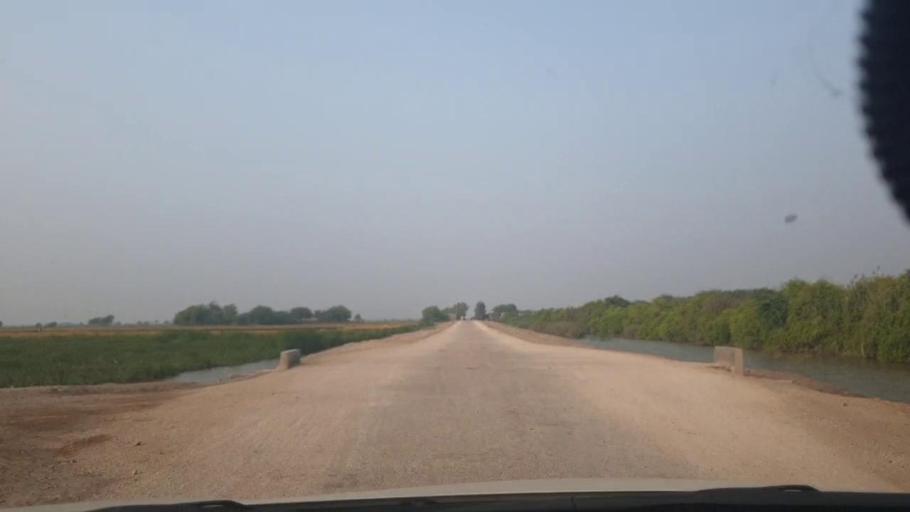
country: PK
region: Sindh
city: Bulri
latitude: 24.8348
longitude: 68.4031
